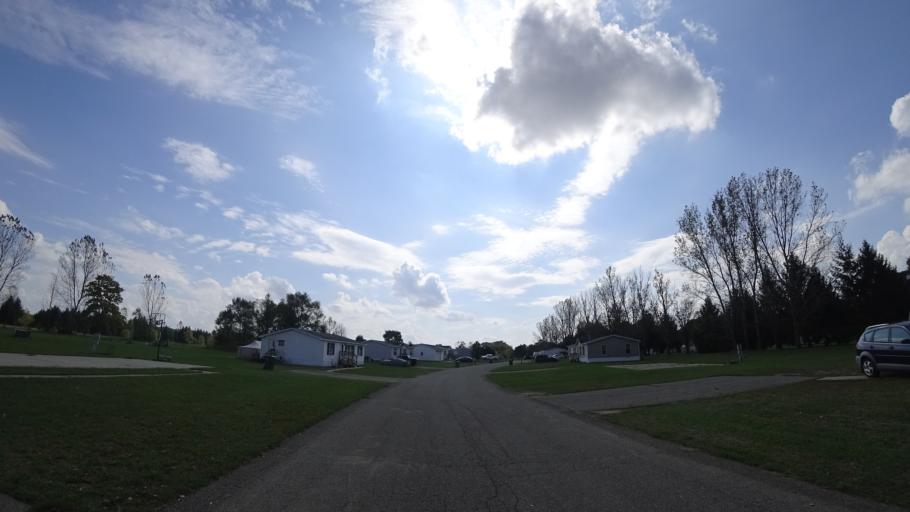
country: US
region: Michigan
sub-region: Saint Joseph County
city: Three Rivers
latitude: 41.9373
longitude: -85.6161
